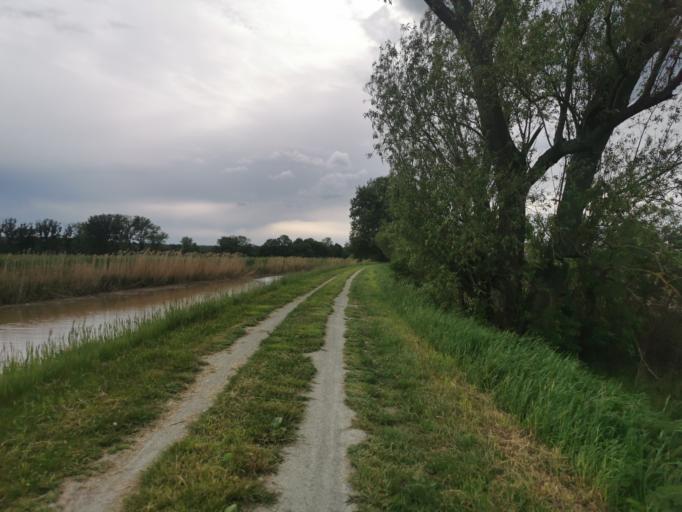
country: SK
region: Trnavsky
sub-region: Okres Skalica
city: Skalica
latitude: 48.8705
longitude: 17.2209
